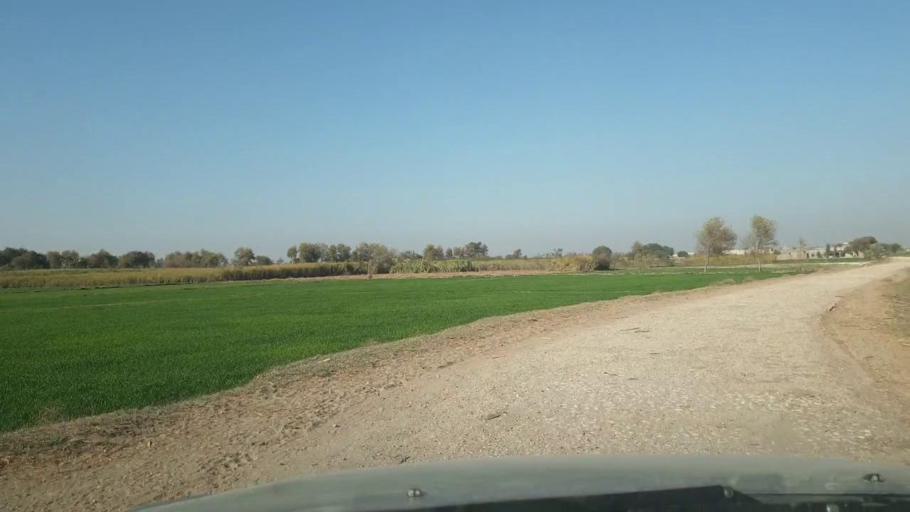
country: PK
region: Sindh
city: Ghotki
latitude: 28.0429
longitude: 69.3348
